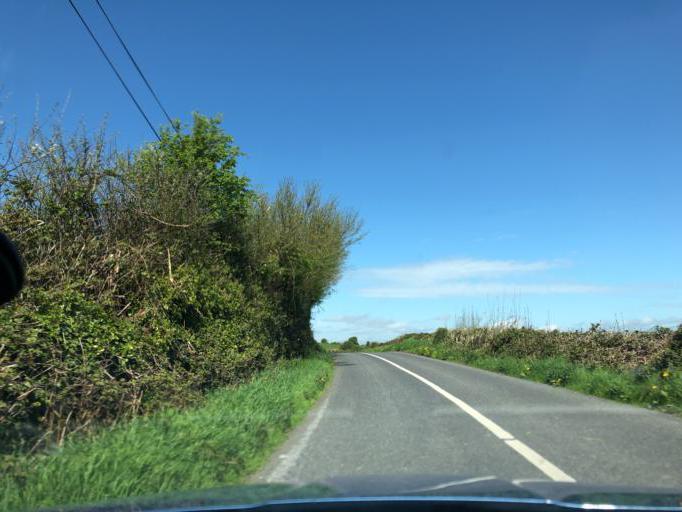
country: IE
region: Connaught
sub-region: County Galway
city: Loughrea
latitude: 53.1608
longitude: -8.3983
